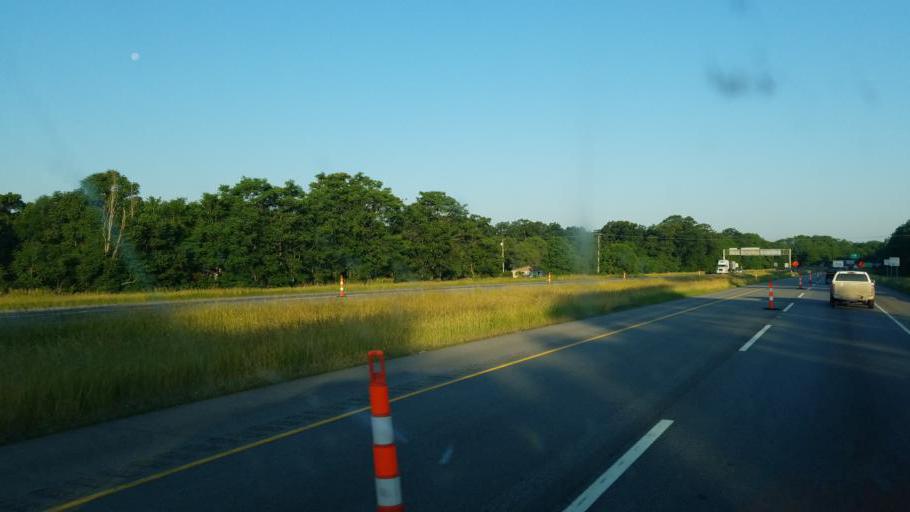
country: US
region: Indiana
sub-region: Porter County
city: Portage
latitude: 41.5809
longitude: -87.1902
